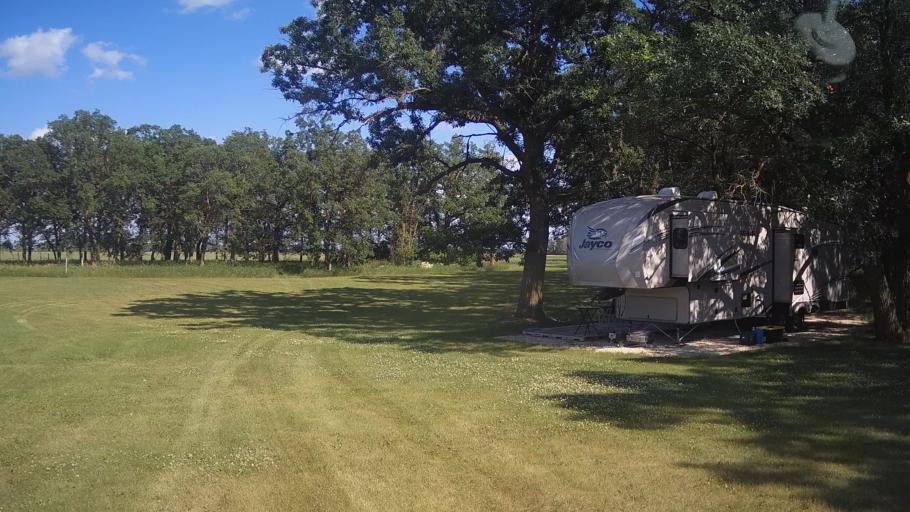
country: CA
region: Manitoba
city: Stonewall
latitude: 50.1248
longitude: -97.4752
